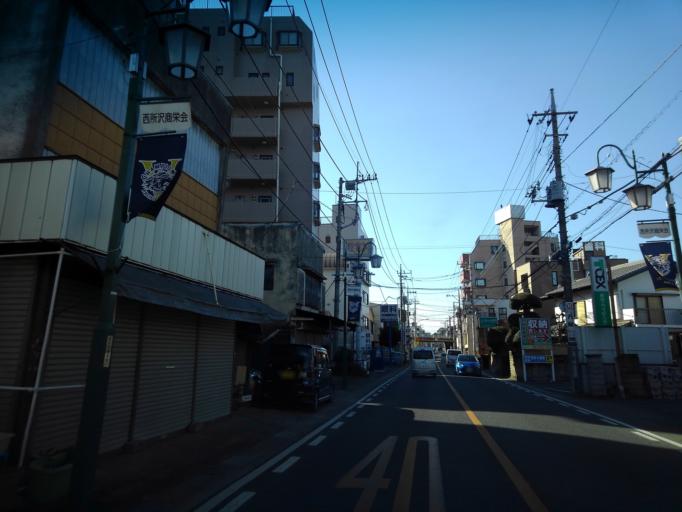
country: JP
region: Saitama
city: Tokorozawa
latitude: 35.7909
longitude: 139.4558
